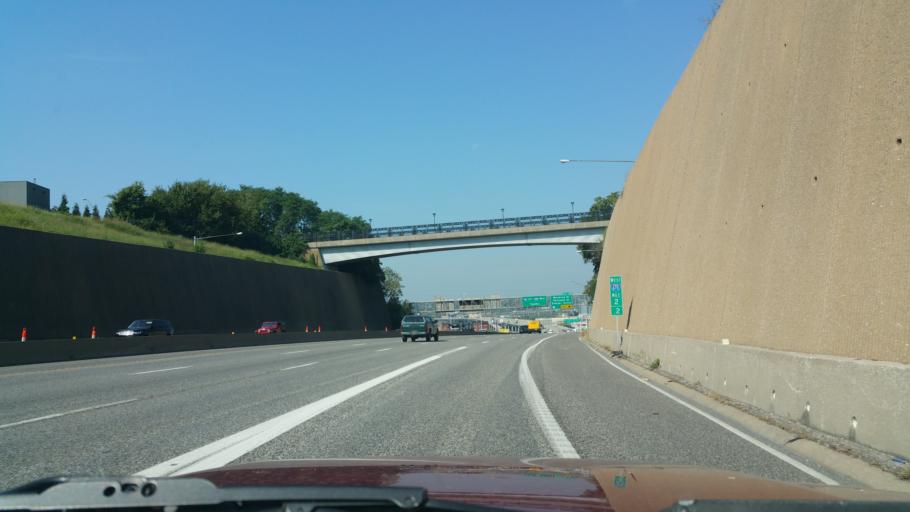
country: US
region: Missouri
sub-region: Jackson County
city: Kansas City
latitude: 39.0966
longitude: -94.5940
